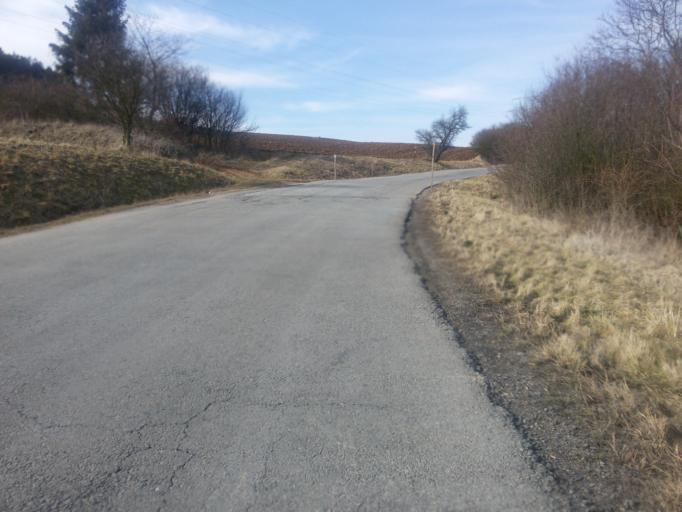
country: CZ
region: South Moravian
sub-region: Okres Brno-Venkov
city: Lomnice
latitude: 49.4158
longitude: 16.4002
